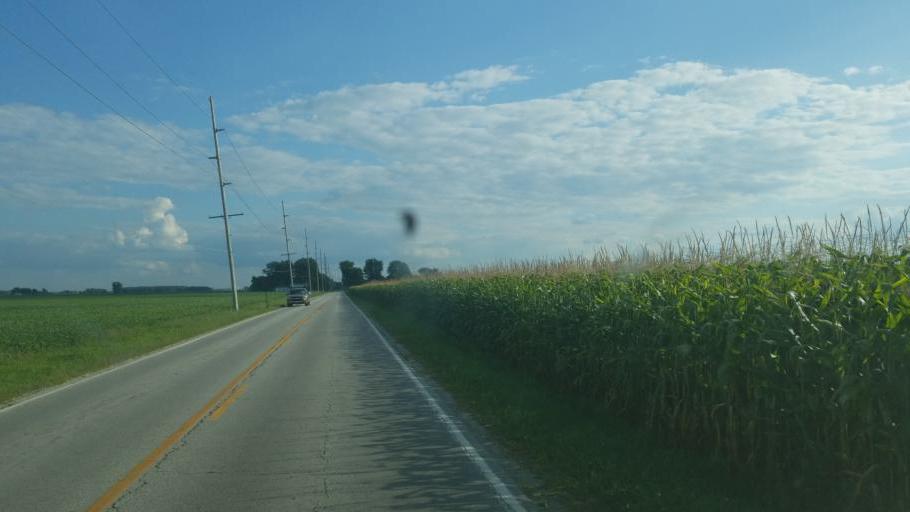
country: US
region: Ohio
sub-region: Sandusky County
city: Ballville
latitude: 41.2915
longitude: -83.1302
